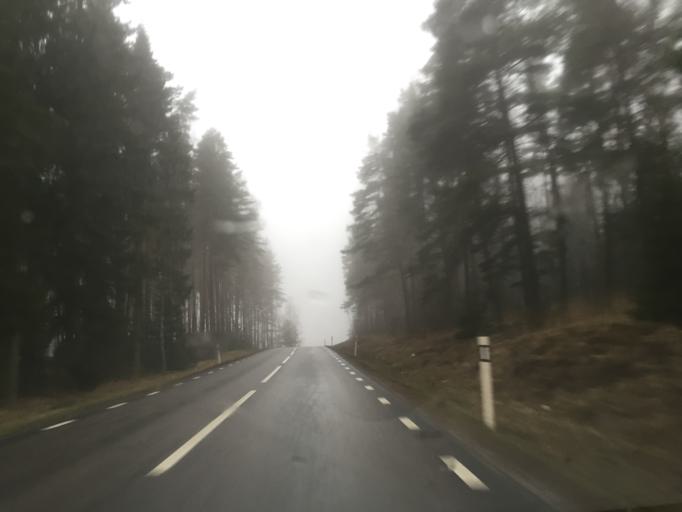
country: SE
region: Soedermanland
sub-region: Flens Kommun
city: Flen
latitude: 58.9140
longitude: 16.4338
